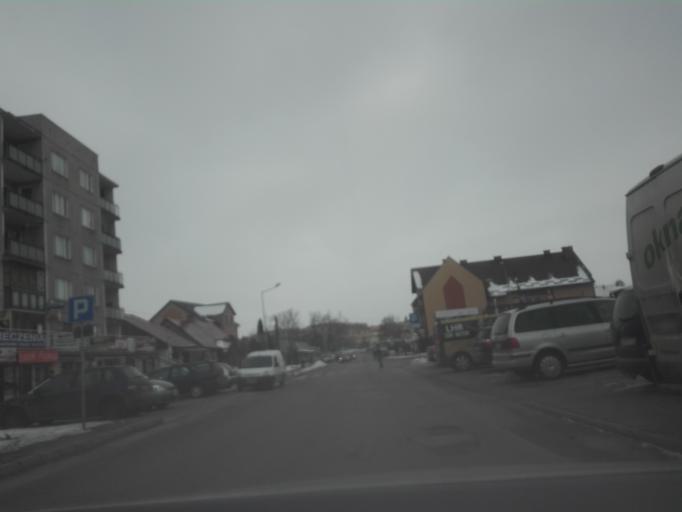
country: PL
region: Lublin Voivodeship
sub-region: Powiat hrubieszowski
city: Hrubieszow
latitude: 50.8054
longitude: 23.8942
